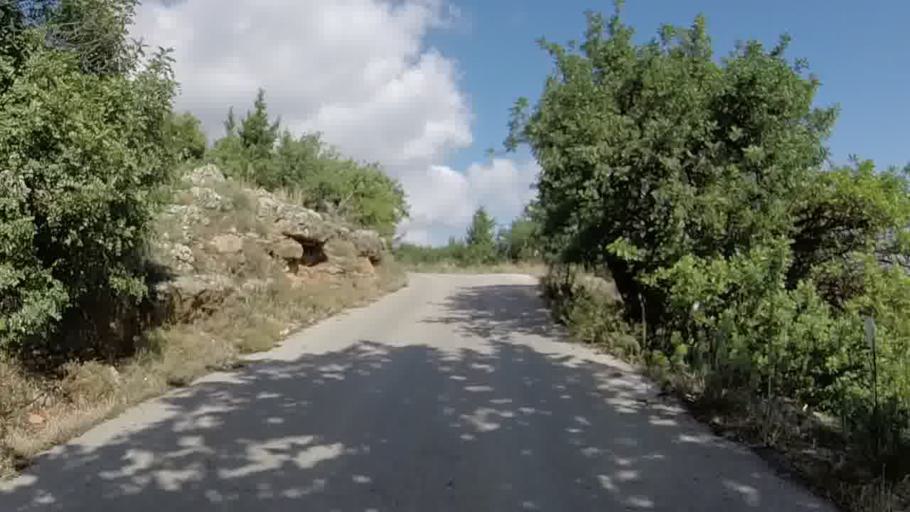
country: GR
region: Crete
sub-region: Nomos Chanias
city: Kalivai
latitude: 35.3881
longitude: 24.1325
